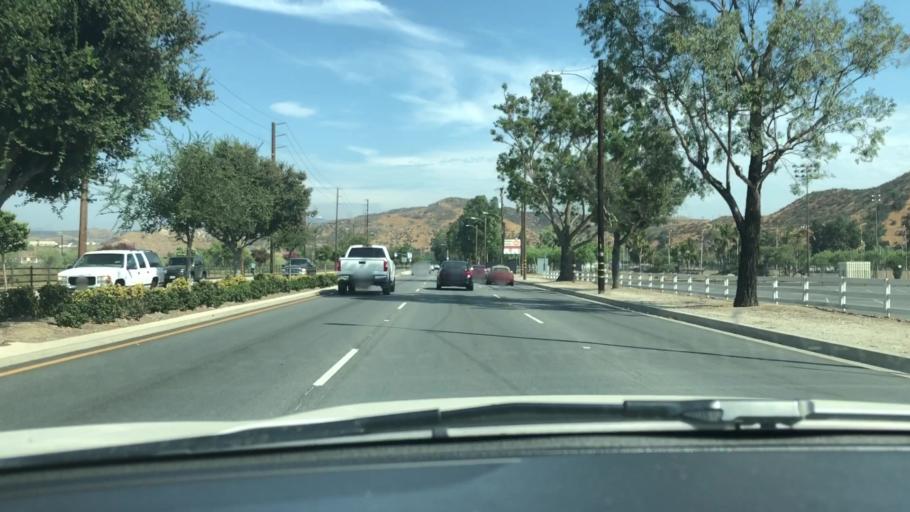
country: US
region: California
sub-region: Los Angeles County
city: Santa Clarita
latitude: 34.4185
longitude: -118.5289
